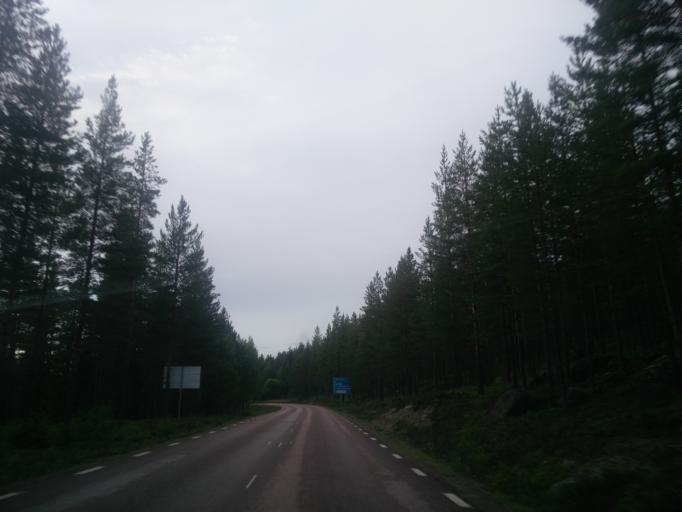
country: NO
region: Hedmark
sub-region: Trysil
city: Innbygda
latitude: 61.7924
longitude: 12.9244
